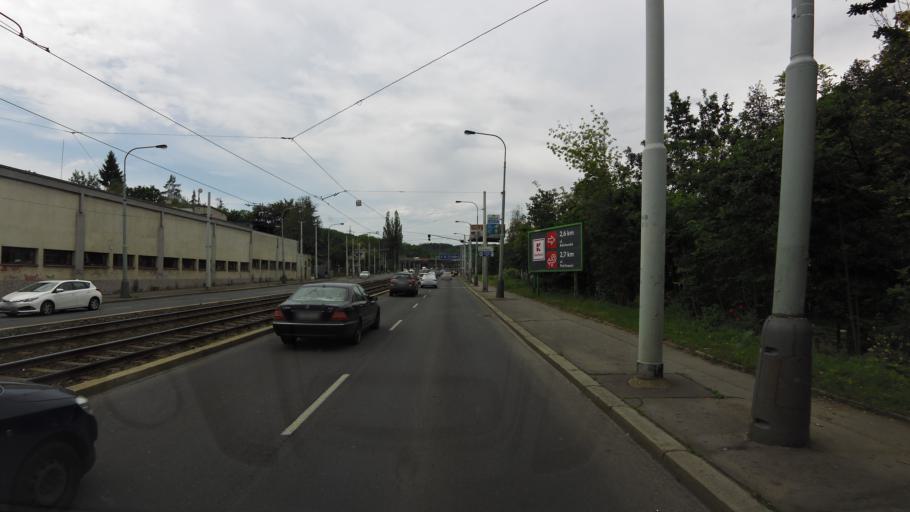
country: CZ
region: Central Bohemia
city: Horomerice
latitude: 50.0678
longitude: 14.3393
